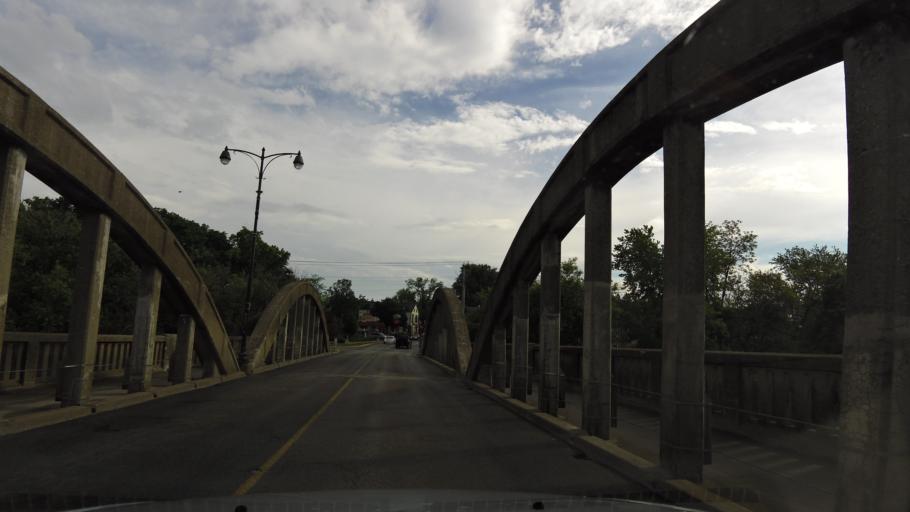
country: CA
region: Ontario
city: Ancaster
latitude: 43.0718
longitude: -79.9528
